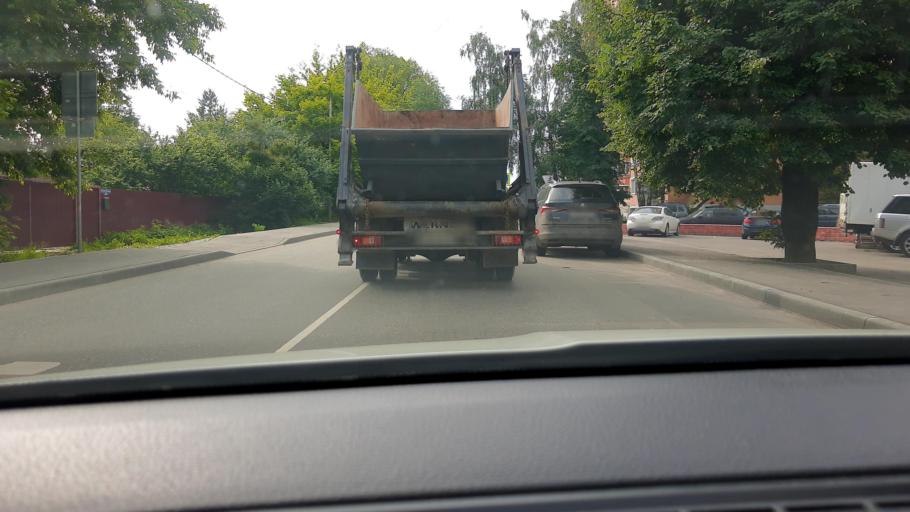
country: RU
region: Moskovskaya
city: Troitsk
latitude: 55.4869
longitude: 37.3074
